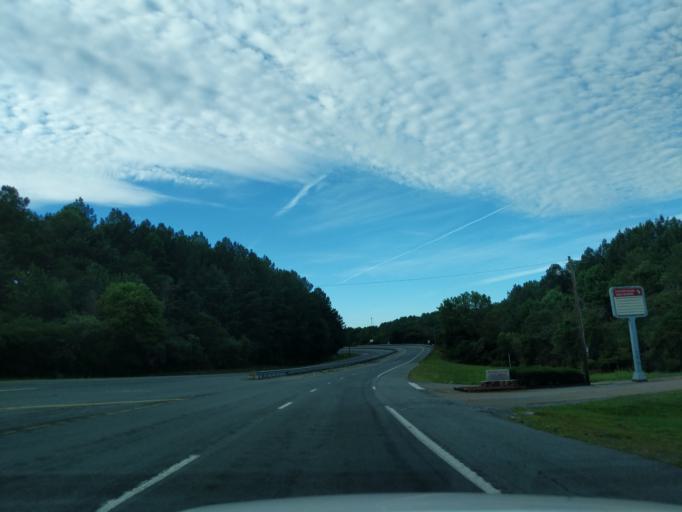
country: US
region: Georgia
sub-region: Fannin County
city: McCaysville
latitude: 35.0234
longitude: -84.3831
